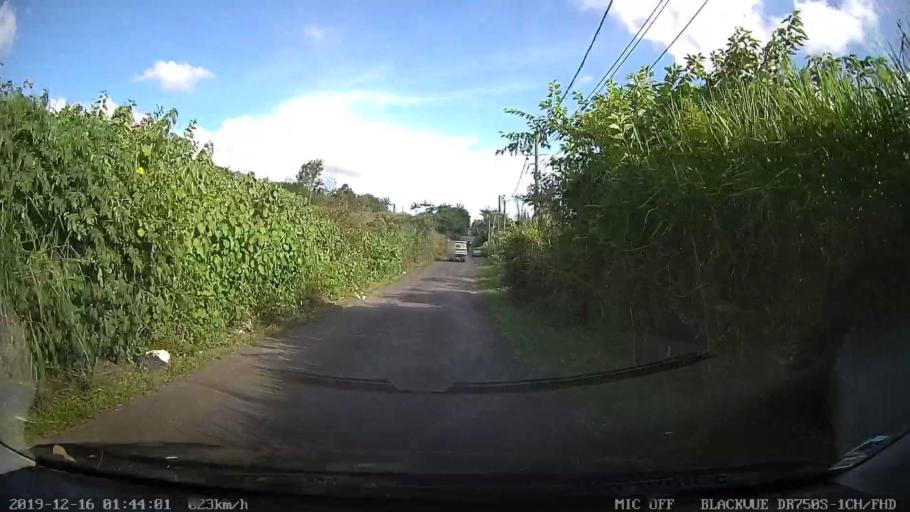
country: RE
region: Reunion
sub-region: Reunion
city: Le Tampon
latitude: -21.2503
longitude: 55.5139
